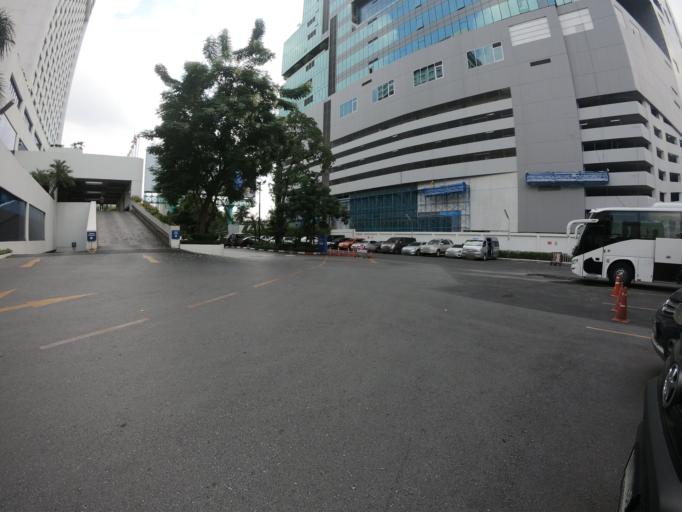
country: TH
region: Bangkok
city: Huai Khwang
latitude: 13.7533
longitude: 100.5717
